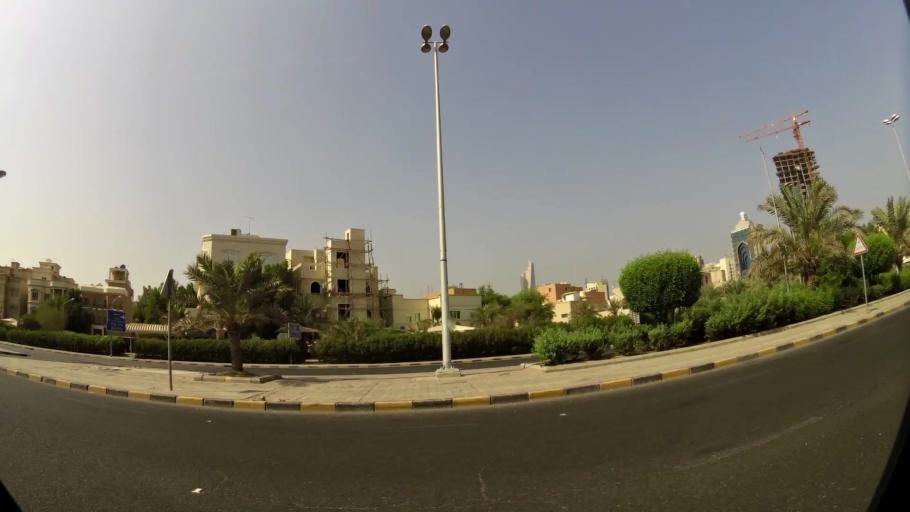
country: KW
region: Al Asimah
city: Ad Dasmah
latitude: 29.3641
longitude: 48.0099
